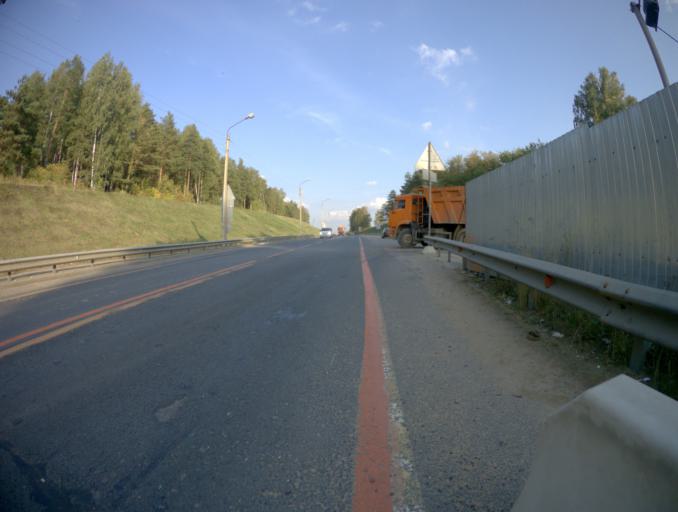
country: RU
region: Vladimir
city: Kameshkovo
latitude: 56.1957
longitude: 40.9134
